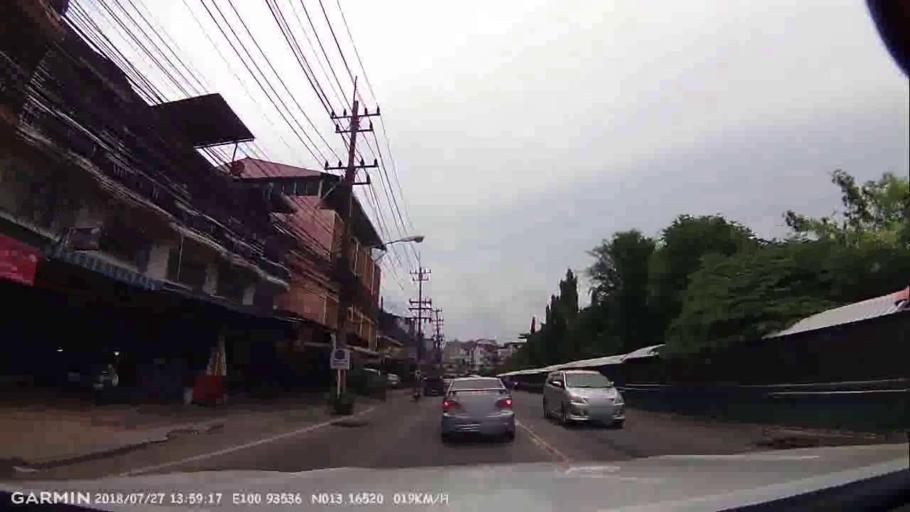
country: TH
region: Chon Buri
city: Si Racha
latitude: 13.1652
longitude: 100.9353
